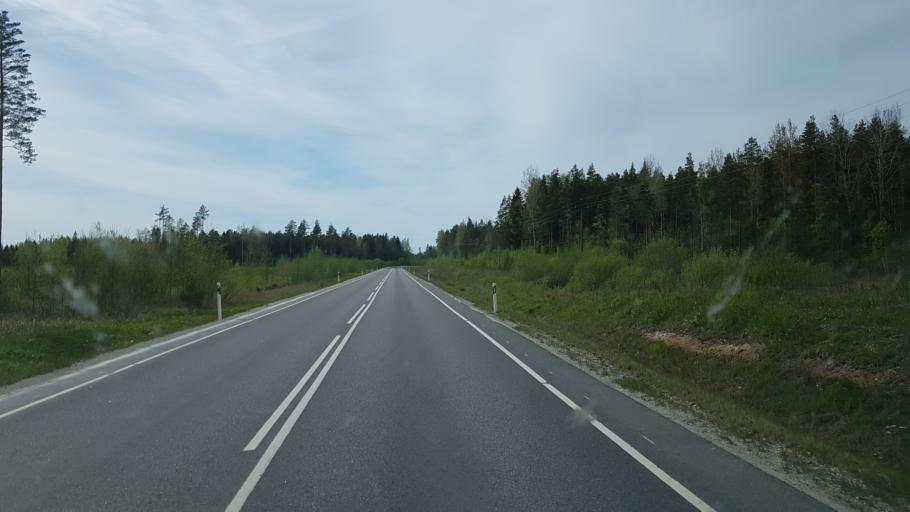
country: EE
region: Ida-Virumaa
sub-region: Johvi vald
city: Johvi
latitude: 59.2983
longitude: 27.4787
